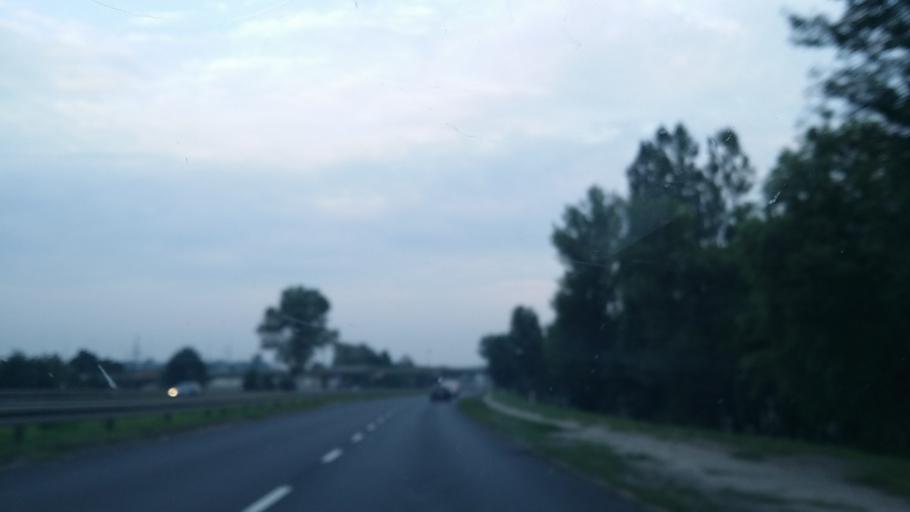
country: PL
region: Lower Silesian Voivodeship
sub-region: Powiat lubinski
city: Lubin
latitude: 51.4093
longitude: 16.2020
